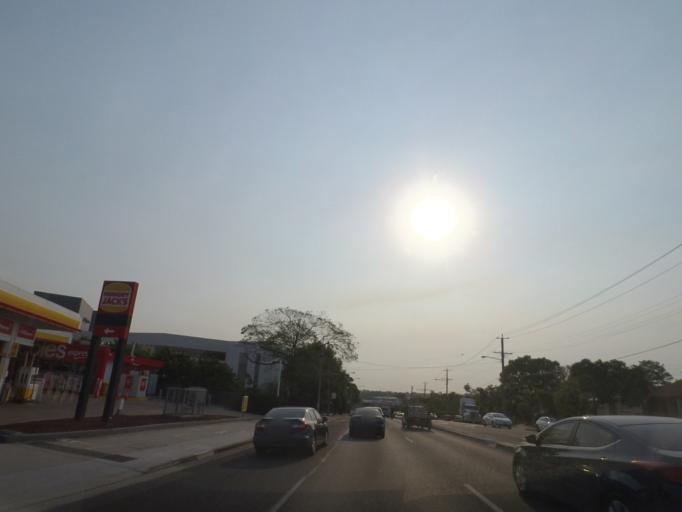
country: AU
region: Queensland
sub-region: Brisbane
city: Upper Mount Gravatt
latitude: -27.5607
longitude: 153.0788
